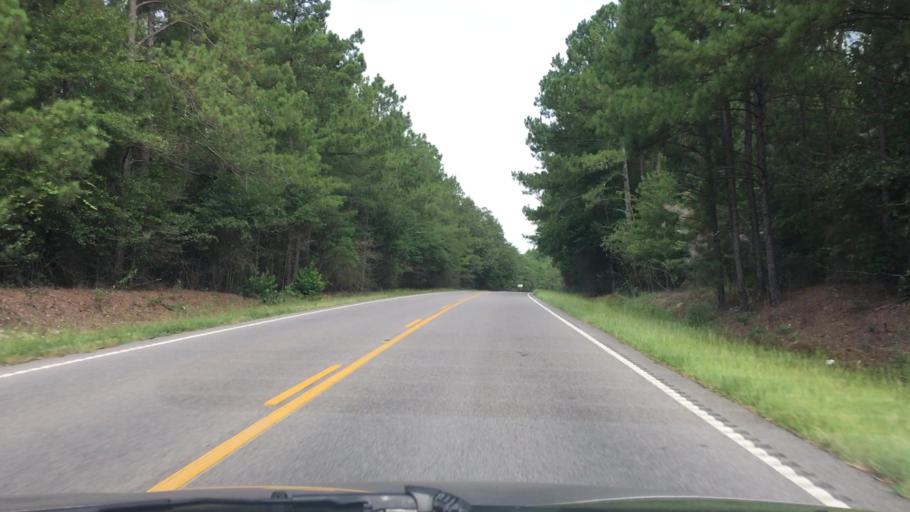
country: US
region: South Carolina
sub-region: Lexington County
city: Leesville
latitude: 33.6764
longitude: -81.4332
